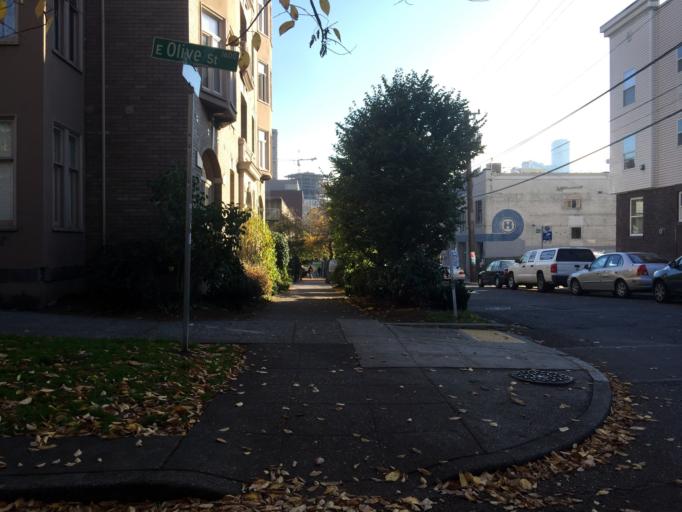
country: US
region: Washington
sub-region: King County
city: Seattle
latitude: 47.6164
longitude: -122.3234
